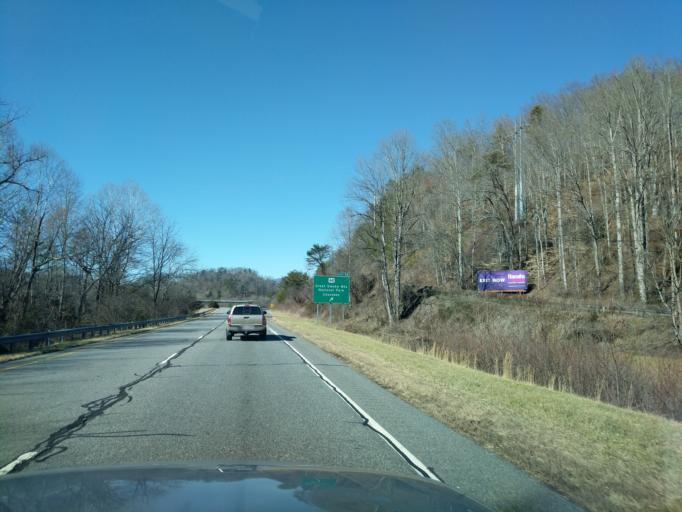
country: US
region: North Carolina
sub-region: Swain County
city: Cherokee
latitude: 35.4186
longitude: -83.3301
